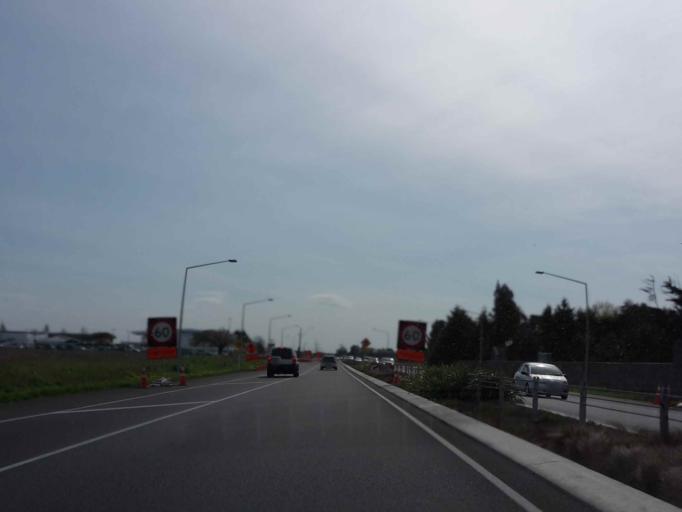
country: NZ
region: Canterbury
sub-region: Selwyn District
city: Prebbleton
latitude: -43.4991
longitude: 172.5464
